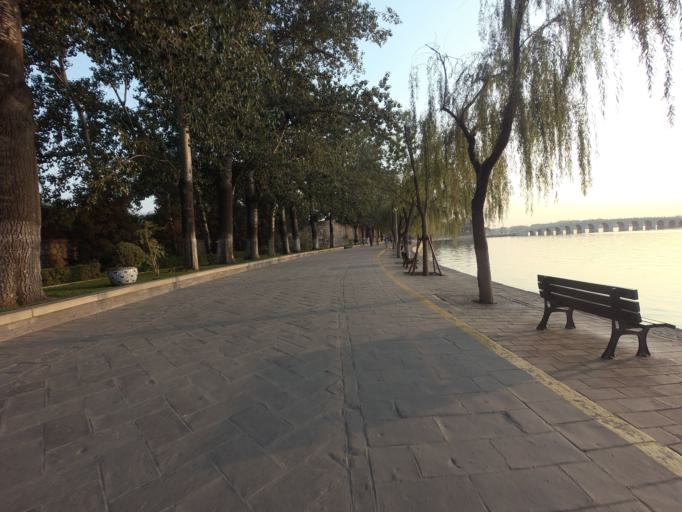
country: CN
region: Beijing
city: Haidian
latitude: 39.9910
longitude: 116.2743
